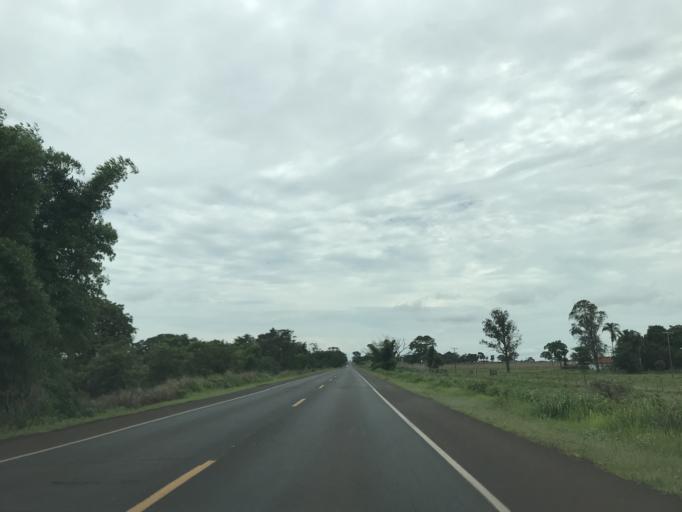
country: BR
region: Minas Gerais
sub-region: Frutal
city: Frutal
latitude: -20.0455
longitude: -49.0507
